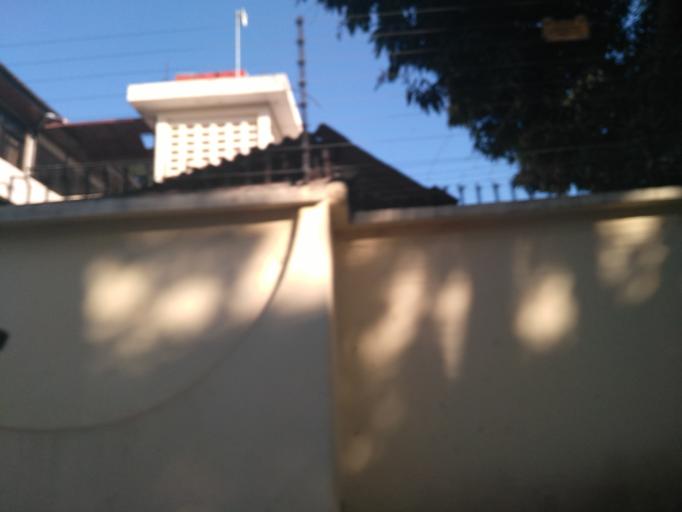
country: TZ
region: Dar es Salaam
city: Magomeni
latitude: -6.7642
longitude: 39.2542
